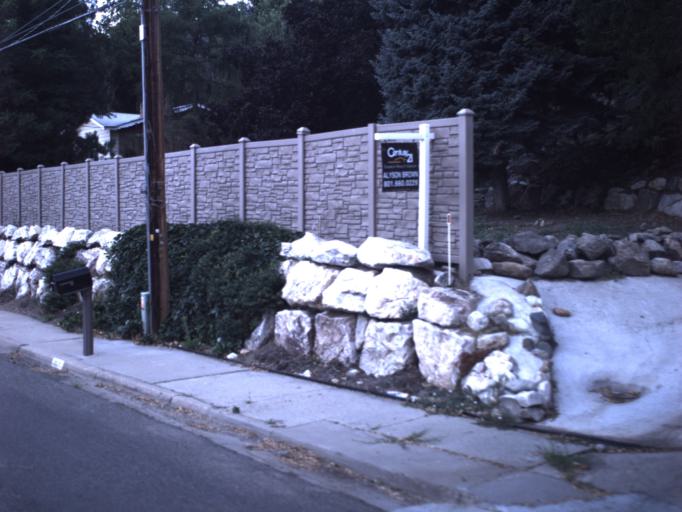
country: US
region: Utah
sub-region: Davis County
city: Farmington
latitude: 40.9600
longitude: -111.8833
